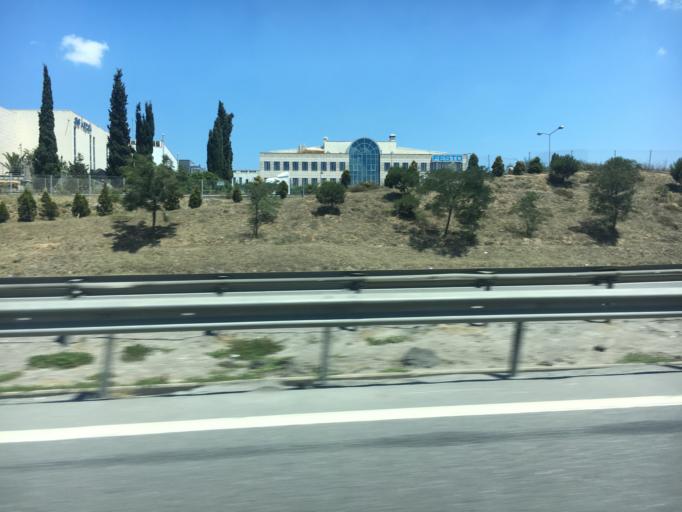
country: TR
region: Kocaeli
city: Balcik
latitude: 40.8823
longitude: 29.3794
